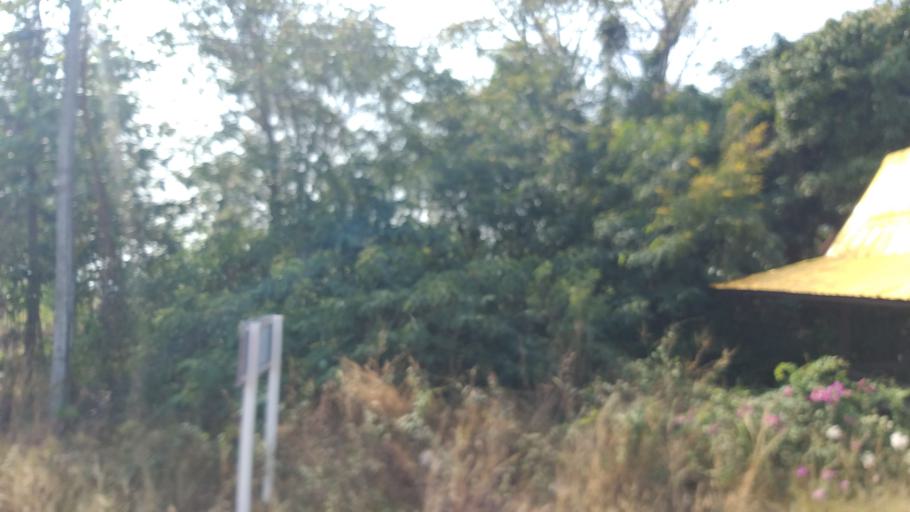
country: TH
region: Changwat Udon Thani
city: Nong Han
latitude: 17.3942
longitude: 103.1855
